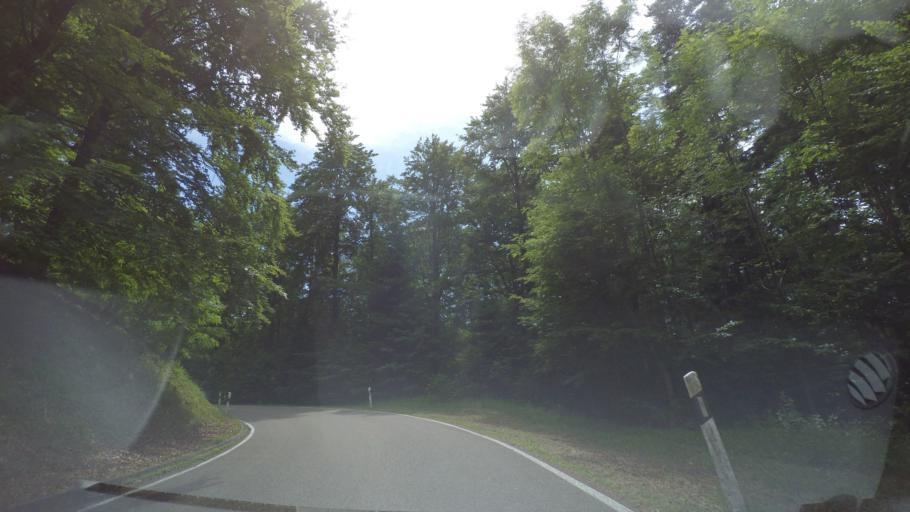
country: DE
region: Baden-Wuerttemberg
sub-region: Regierungsbezirk Stuttgart
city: Kaisersbach
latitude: 48.9414
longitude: 9.6664
